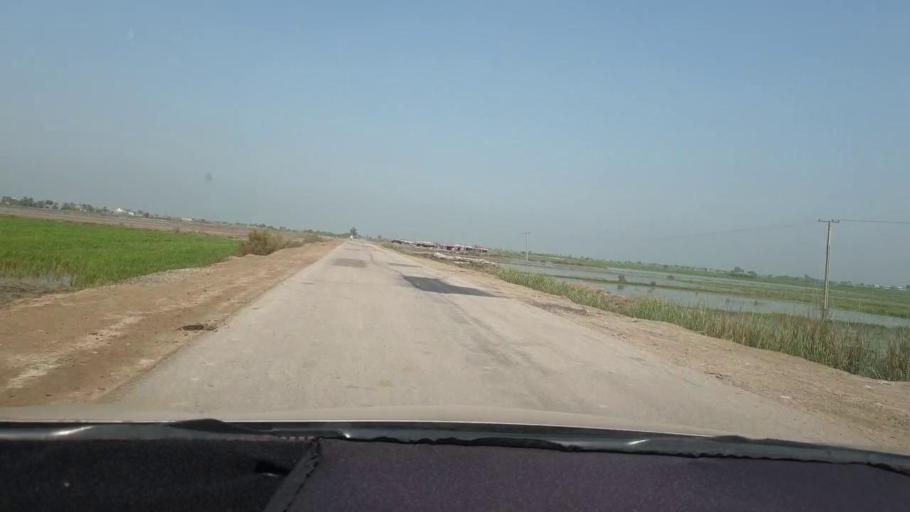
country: PK
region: Sindh
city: Miro Khan
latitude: 27.8329
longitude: 68.0133
